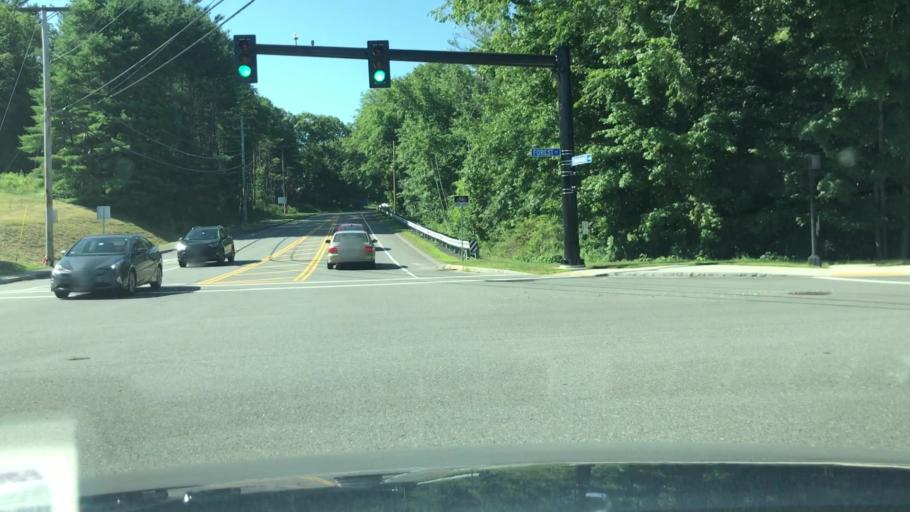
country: US
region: Massachusetts
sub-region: Middlesex County
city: Marlborough
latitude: 42.3316
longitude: -71.5859
